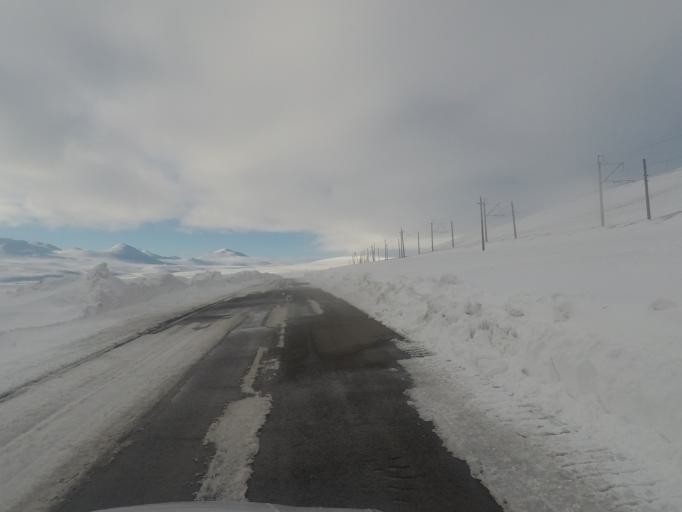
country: GE
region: Kvemo Kartli
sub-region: Tsalka
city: Tsalka
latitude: 41.4691
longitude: 43.8563
